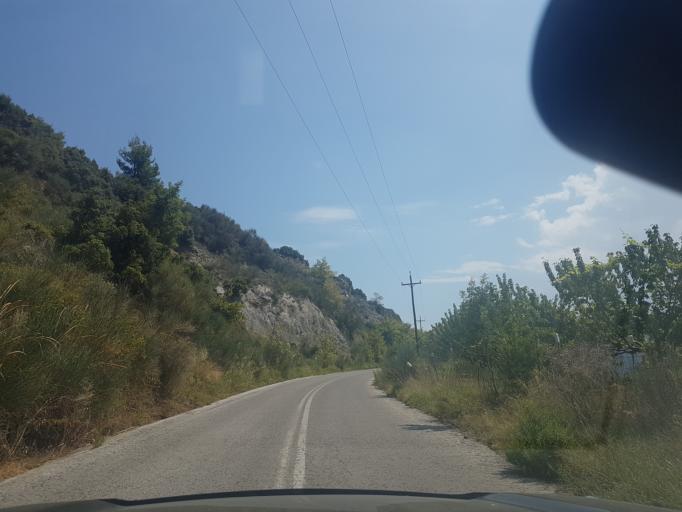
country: GR
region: Central Greece
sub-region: Nomos Evvoias
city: Yimnon
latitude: 38.6397
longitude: 23.8921
